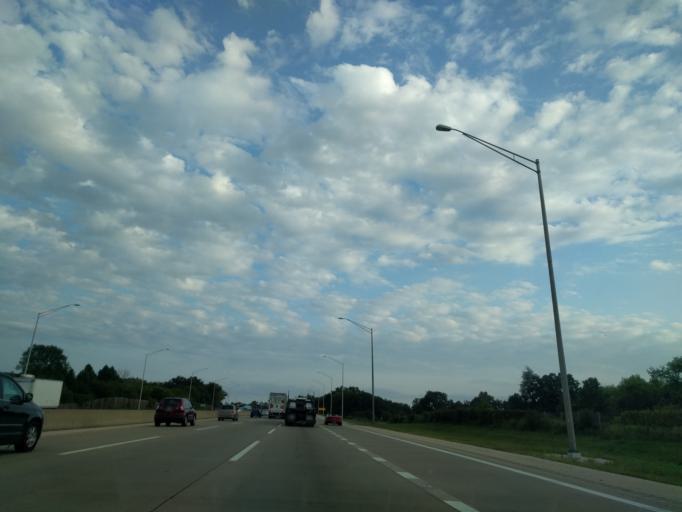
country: US
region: Illinois
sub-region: Lake County
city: Wadsworth
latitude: 42.4394
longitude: -87.9563
